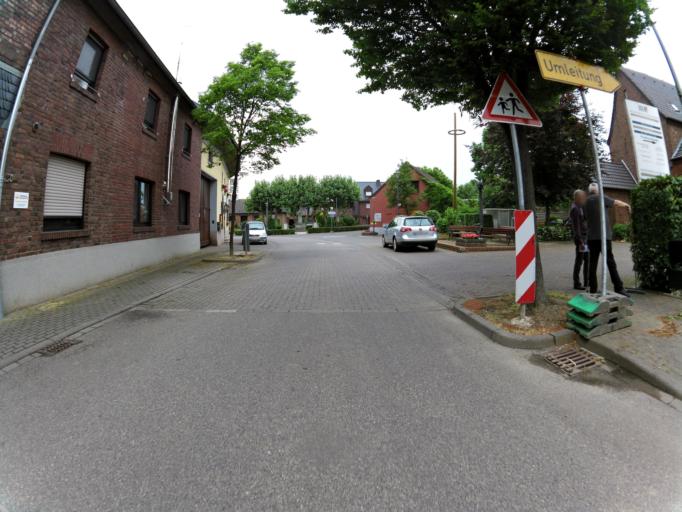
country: DE
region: North Rhine-Westphalia
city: Geilenkirchen
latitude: 50.9841
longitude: 6.1861
